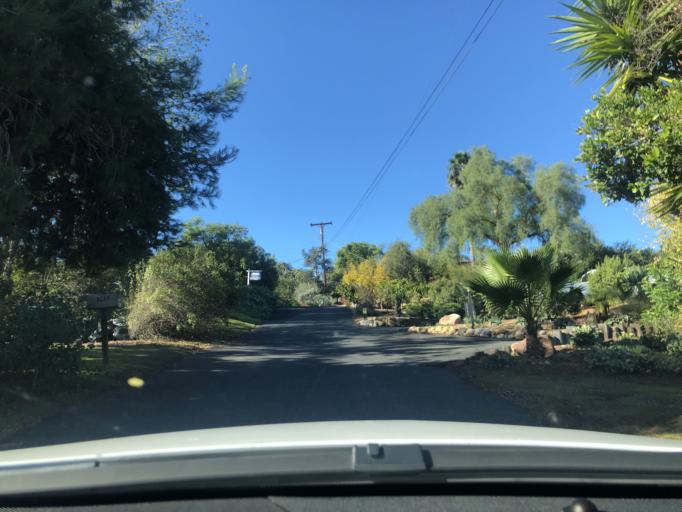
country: US
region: California
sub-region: San Diego County
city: Rancho San Diego
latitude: 32.7711
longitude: -116.9410
